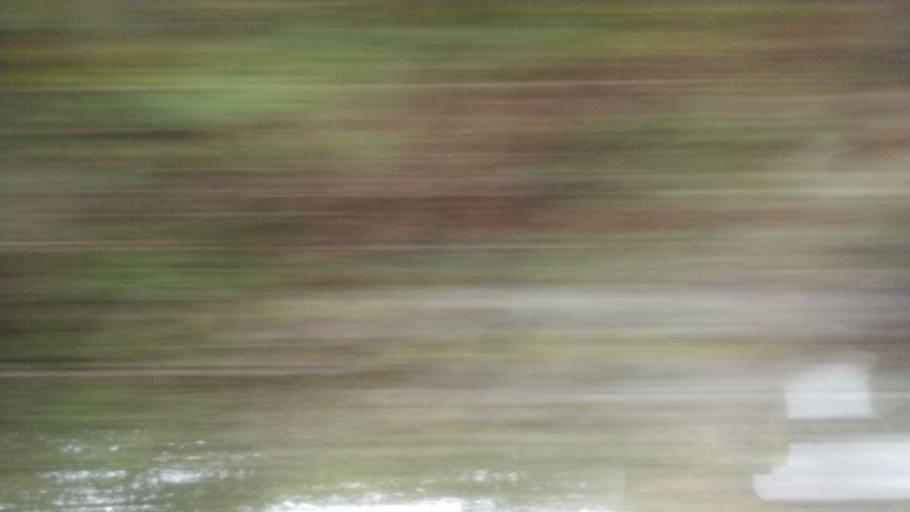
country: GB
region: England
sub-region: Lancashire
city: Appley Bridge
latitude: 53.5701
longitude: -2.7127
